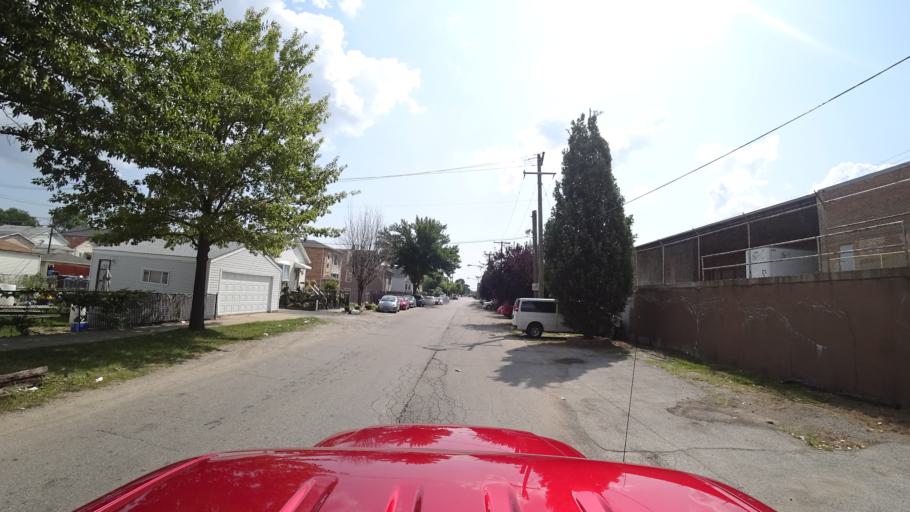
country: US
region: Illinois
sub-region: Cook County
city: Chicago
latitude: 41.8273
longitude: -87.6970
